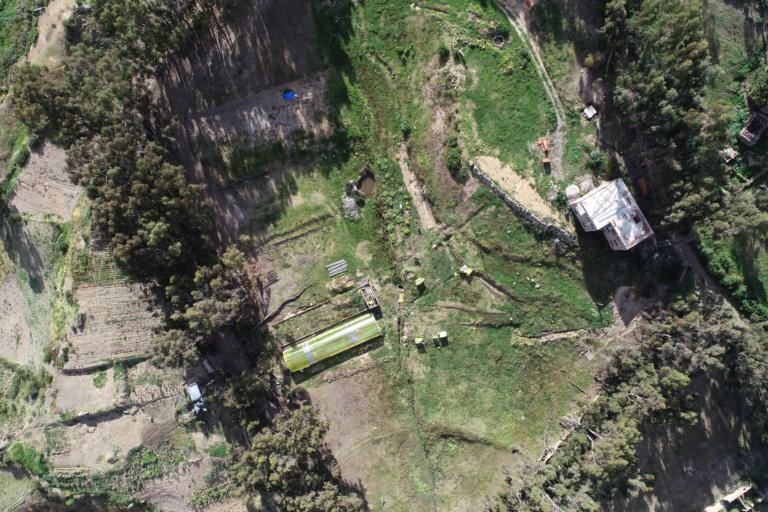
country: BO
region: La Paz
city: La Paz
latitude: -16.5503
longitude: -67.9928
